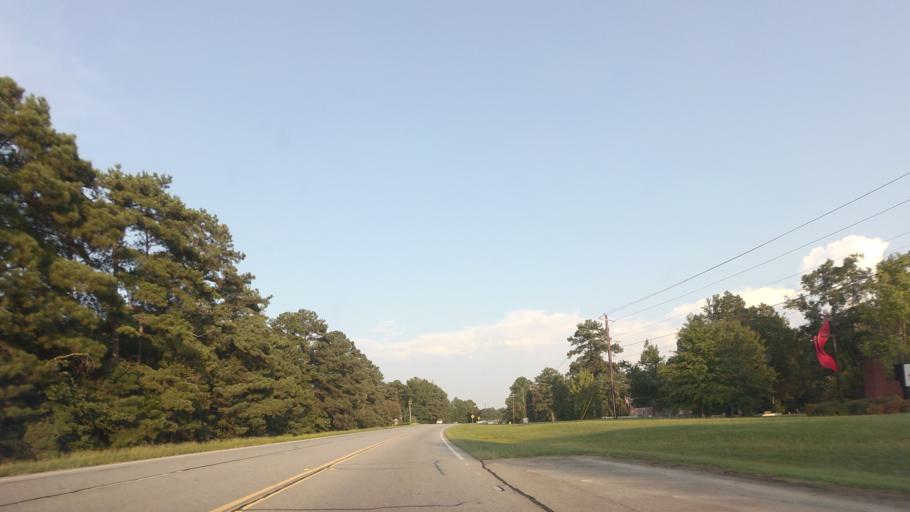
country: US
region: Georgia
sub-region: Bibb County
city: West Point
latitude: 32.8518
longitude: -83.7633
